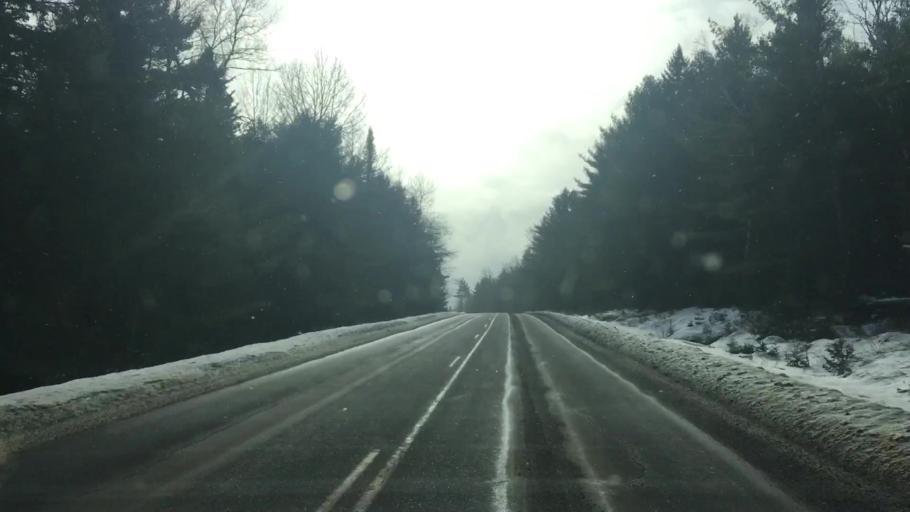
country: US
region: Maine
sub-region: Washington County
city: Calais
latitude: 45.0691
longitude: -67.3311
